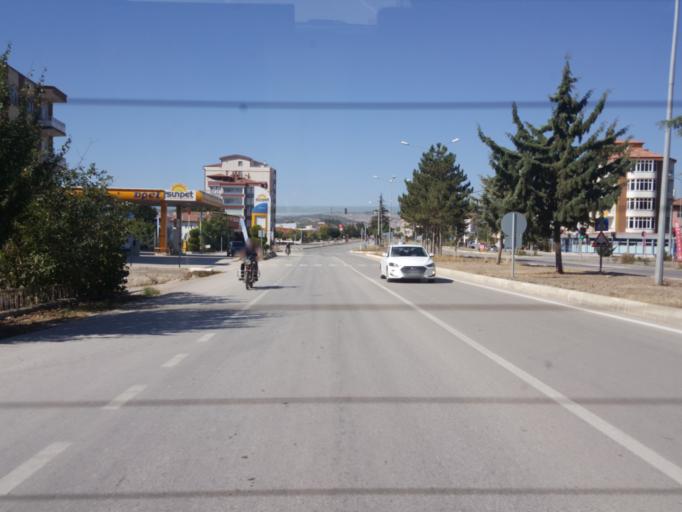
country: TR
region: Tokat
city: Zile
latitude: 40.2929
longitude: 35.8871
